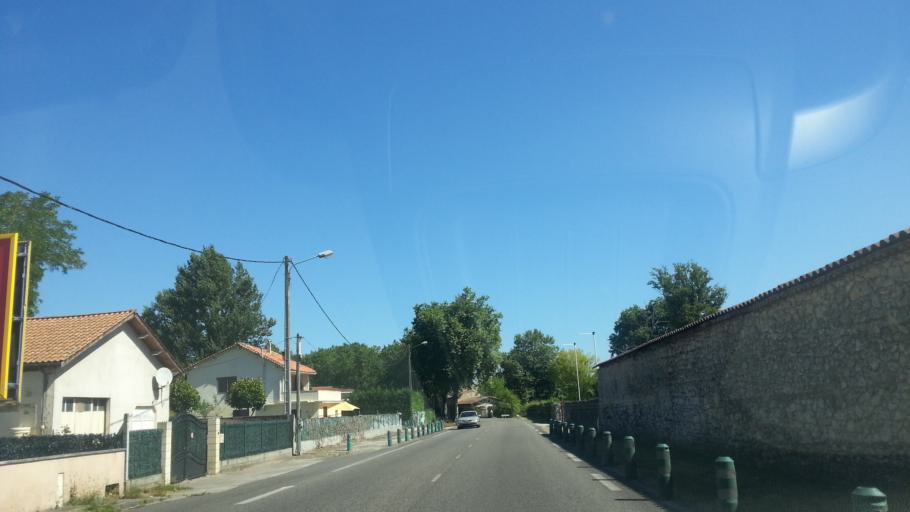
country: FR
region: Aquitaine
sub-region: Departement de la Gironde
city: Martillac
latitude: 44.6973
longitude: -0.5117
